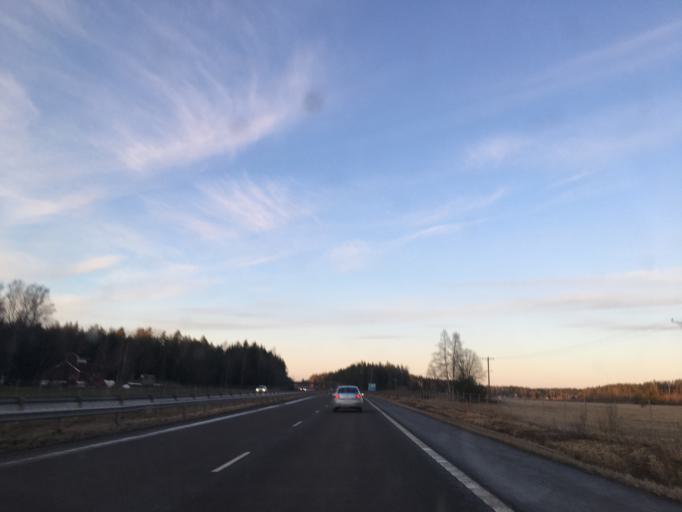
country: FI
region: Varsinais-Suomi
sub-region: Turku
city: Turku
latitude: 60.5211
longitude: 22.3047
